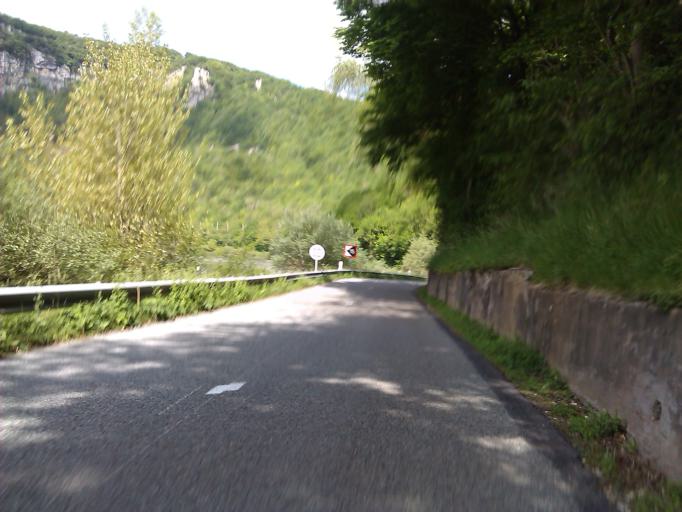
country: FR
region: Franche-Comte
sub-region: Departement du Doubs
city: Roulans
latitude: 47.3026
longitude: 6.2155
